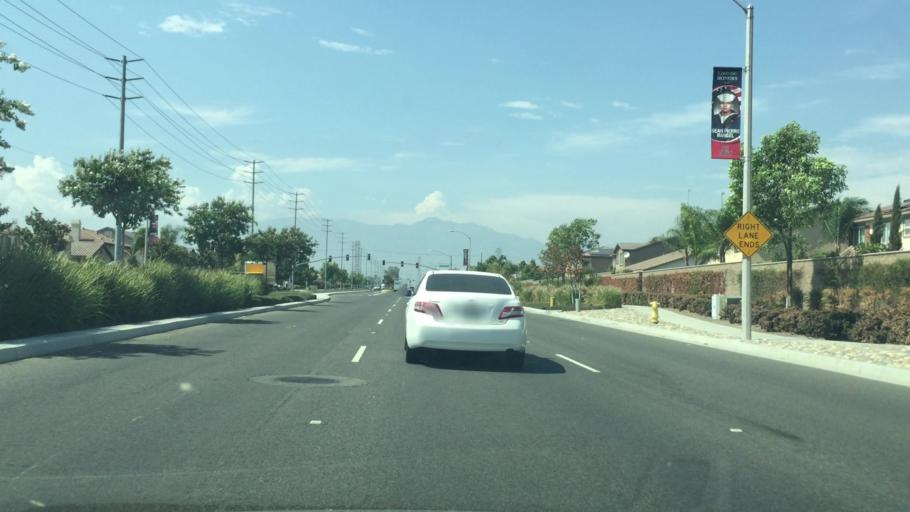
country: US
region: California
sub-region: Riverside County
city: Norco
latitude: 33.9626
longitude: -117.5930
